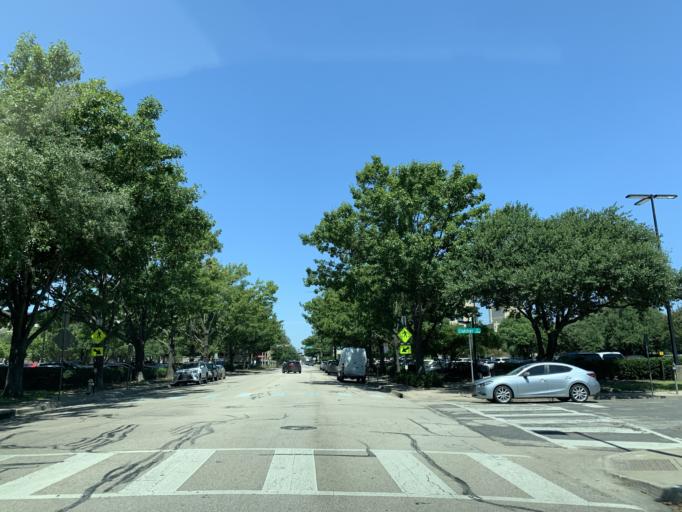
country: US
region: Texas
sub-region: Dallas County
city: Dallas
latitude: 32.7891
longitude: -96.7759
